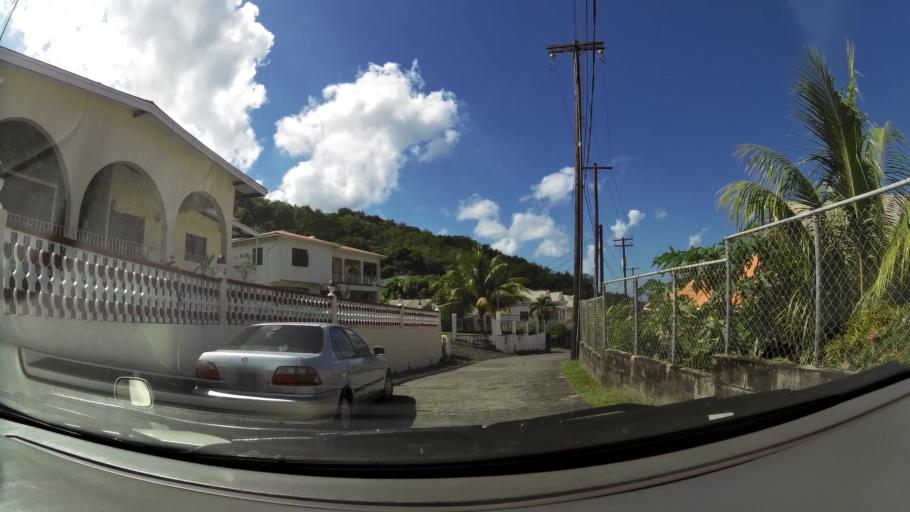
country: VC
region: Saint George
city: Kingstown Park
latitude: 13.1709
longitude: -61.2400
